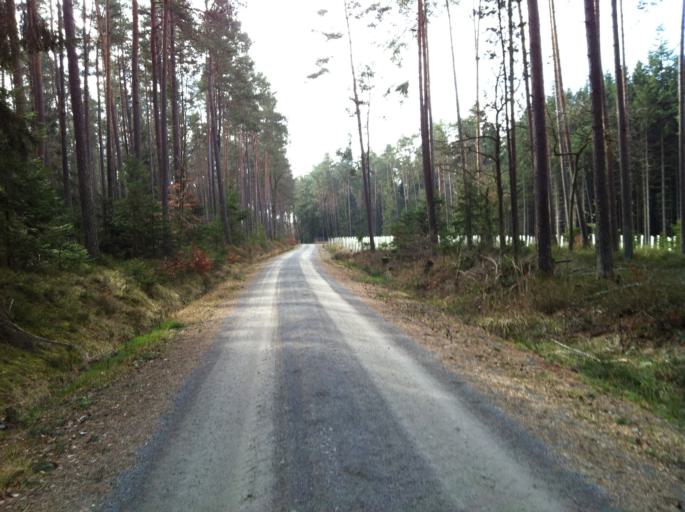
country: DE
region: Hesse
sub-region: Regierungsbezirk Darmstadt
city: Erbach
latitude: 49.6454
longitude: 8.9506
